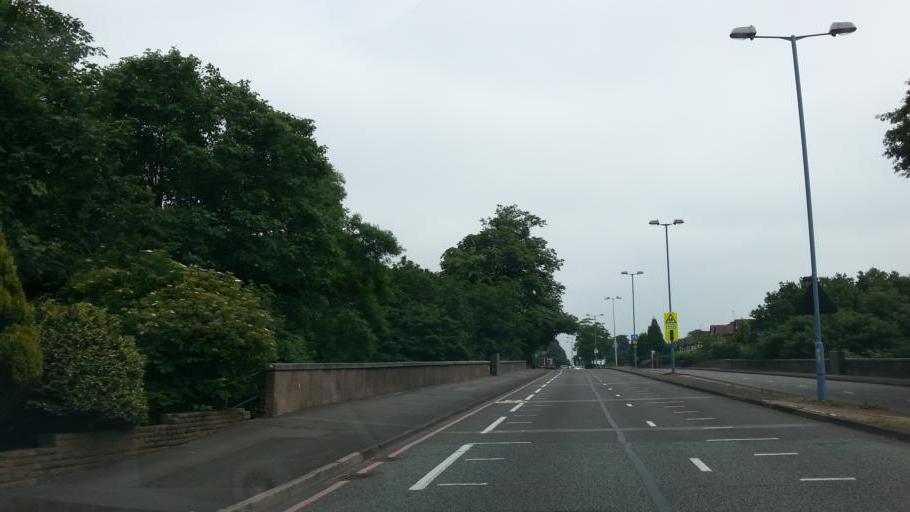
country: GB
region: England
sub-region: Sandwell
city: West Bromwich
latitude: 52.5437
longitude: -1.9492
